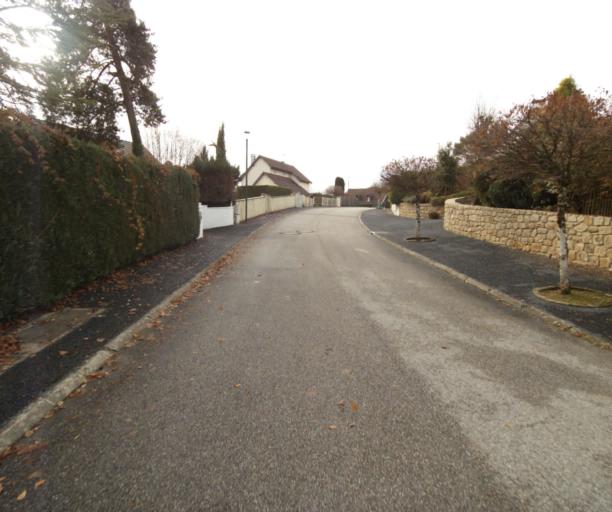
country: FR
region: Limousin
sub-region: Departement de la Correze
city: Chameyrat
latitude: 45.2598
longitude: 1.7031
